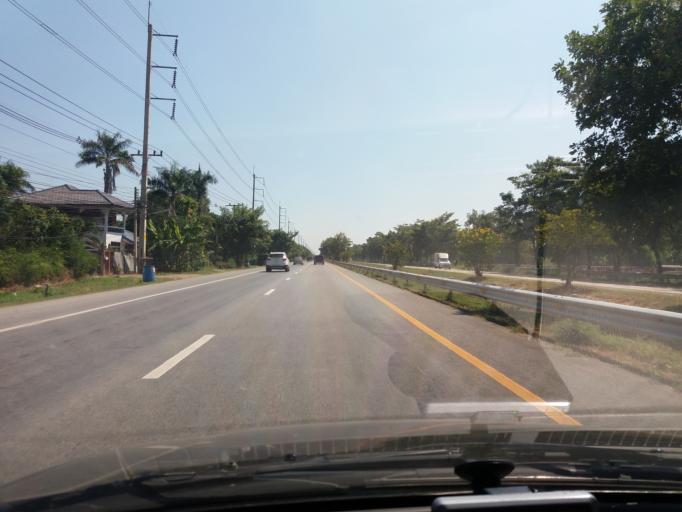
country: TH
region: Chai Nat
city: Chai Nat
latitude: 15.1378
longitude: 100.1436
